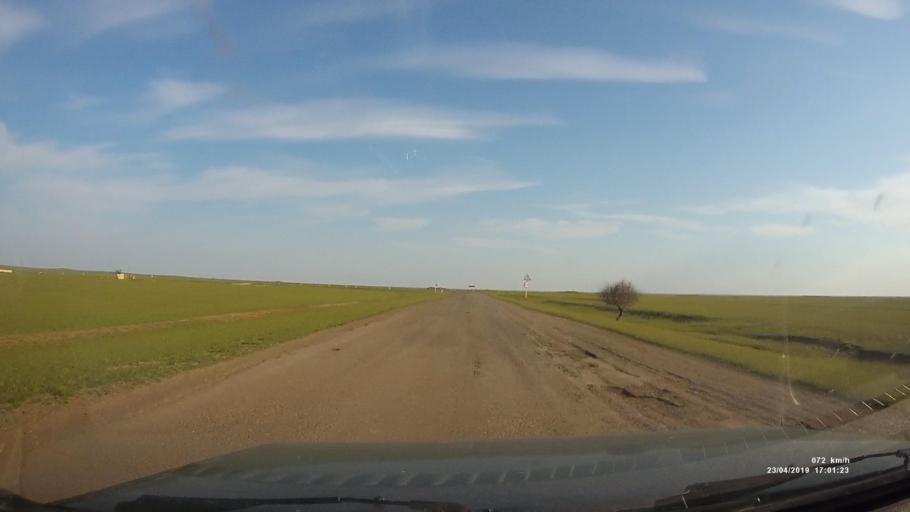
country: RU
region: Kalmykiya
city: Priyutnoye
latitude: 46.2966
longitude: 43.4079
